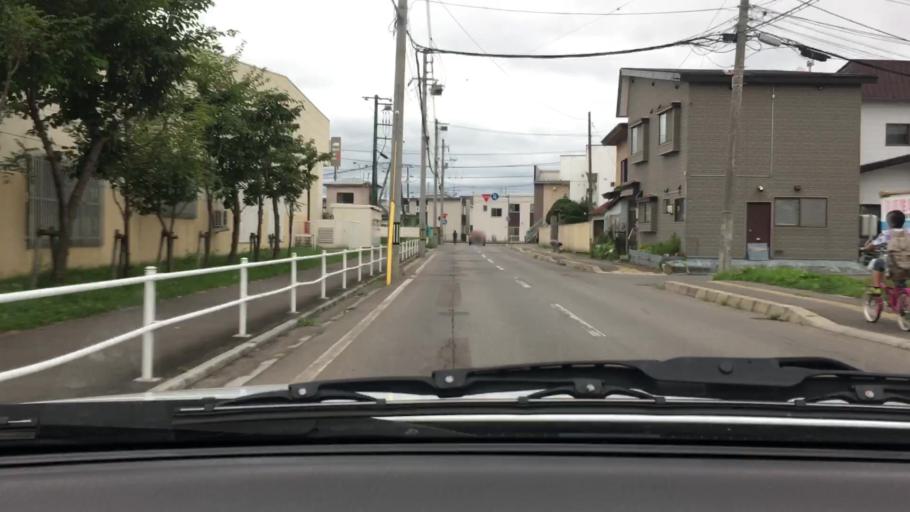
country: JP
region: Hokkaido
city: Hakodate
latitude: 41.8018
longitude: 140.7310
